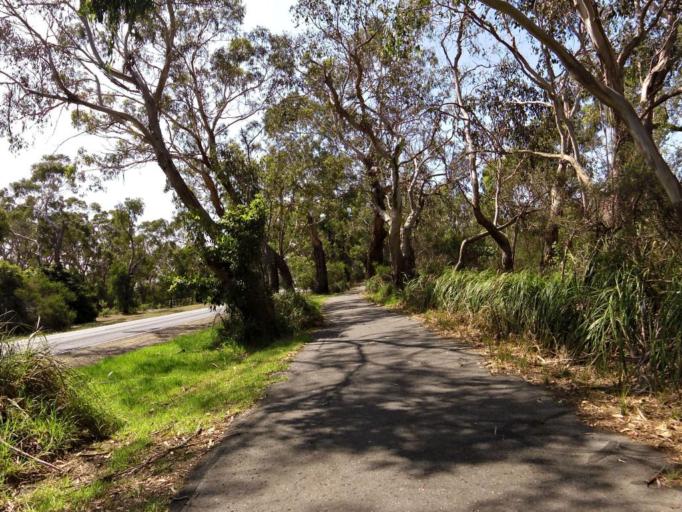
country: AU
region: Victoria
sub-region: Mornington Peninsula
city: Crib Point
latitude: -38.3309
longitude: 145.1821
